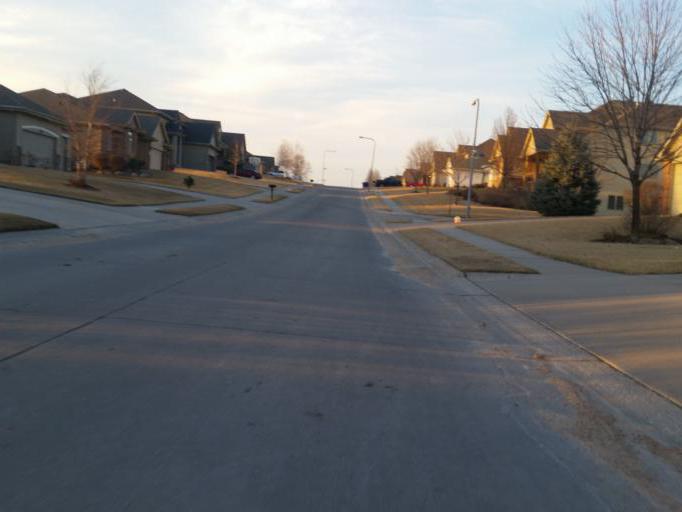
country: US
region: Nebraska
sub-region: Sarpy County
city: Papillion
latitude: 41.1551
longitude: -95.9999
